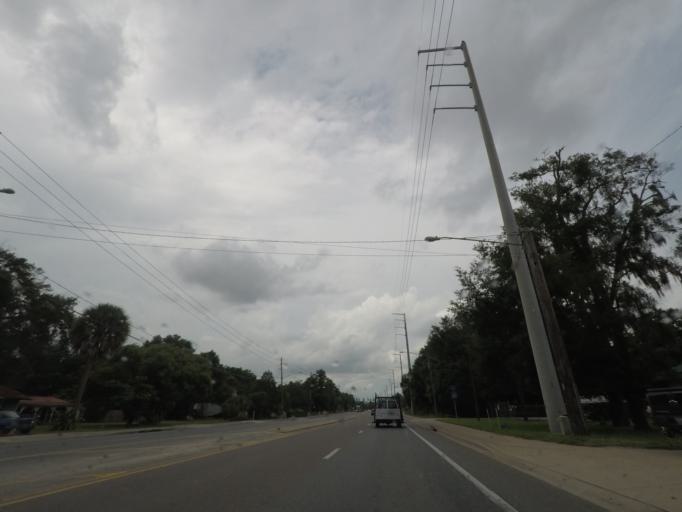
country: US
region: Florida
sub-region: Polk County
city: Loughman
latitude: 28.2411
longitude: -81.5651
